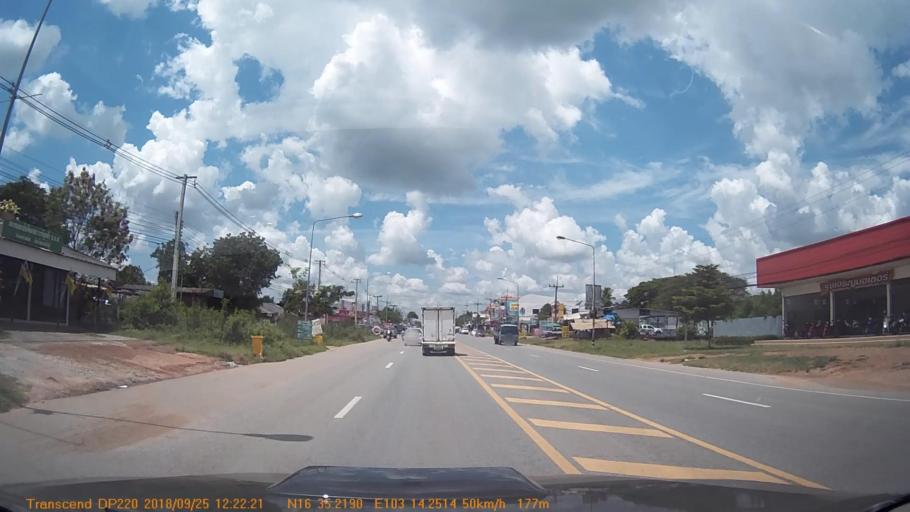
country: TH
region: Kalasin
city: Huai Mek
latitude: 16.5869
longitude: 103.2376
